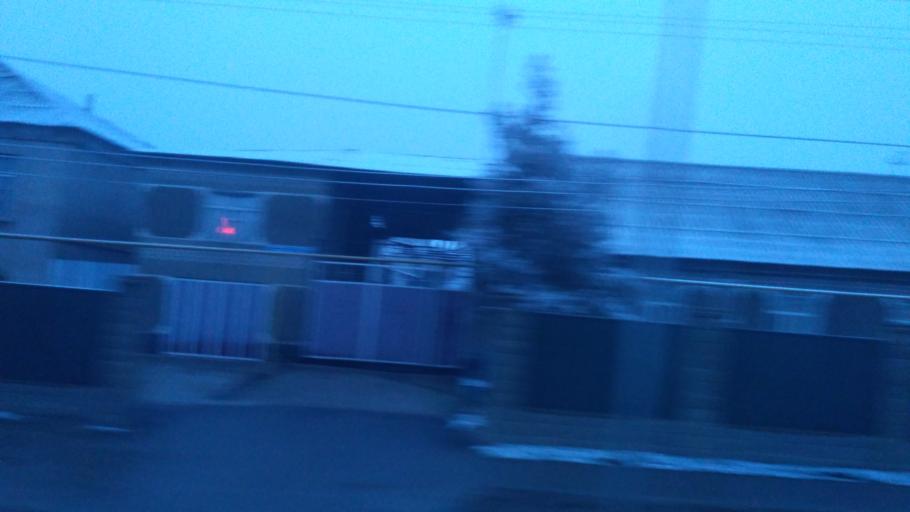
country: KZ
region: Ongtustik Qazaqstan
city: Shymkent
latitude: 42.3696
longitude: 69.5083
